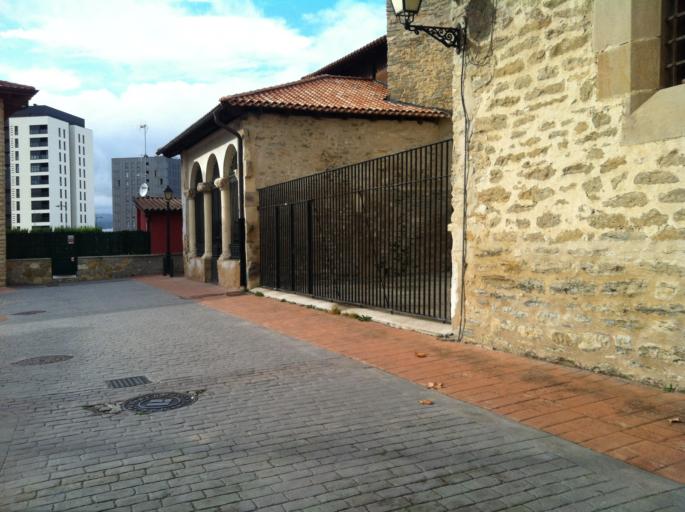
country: ES
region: Basque Country
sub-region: Provincia de Alava
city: Gasteiz / Vitoria
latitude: 42.8516
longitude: -2.7053
